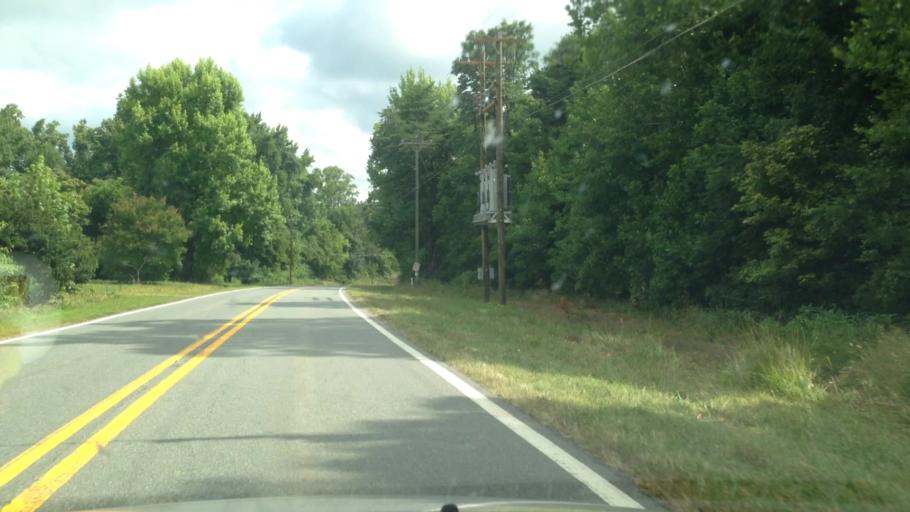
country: US
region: North Carolina
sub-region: Rockingham County
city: Reidsville
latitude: 36.4304
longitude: -79.5805
